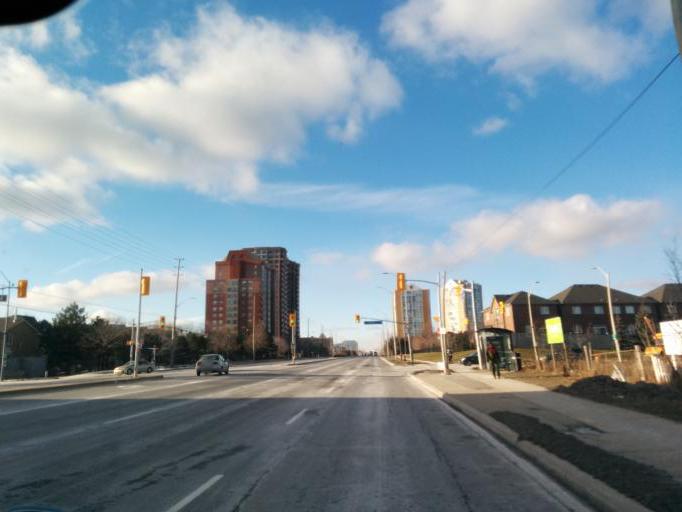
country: CA
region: Ontario
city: Mississauga
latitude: 43.6089
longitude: -79.6559
